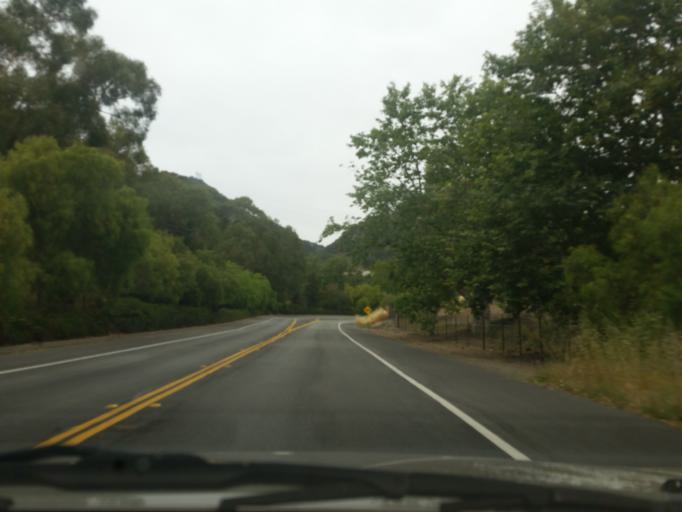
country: US
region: California
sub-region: San Luis Obispo County
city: Avila Beach
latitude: 35.1914
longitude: -120.7181
